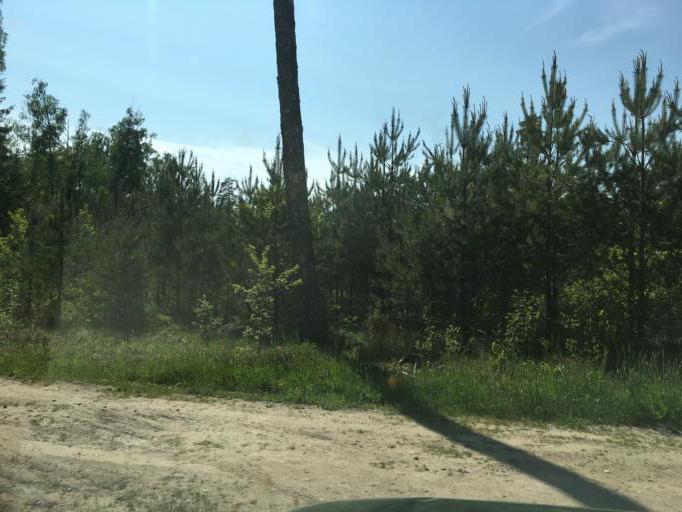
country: LV
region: Dundaga
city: Dundaga
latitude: 57.4327
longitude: 22.3148
